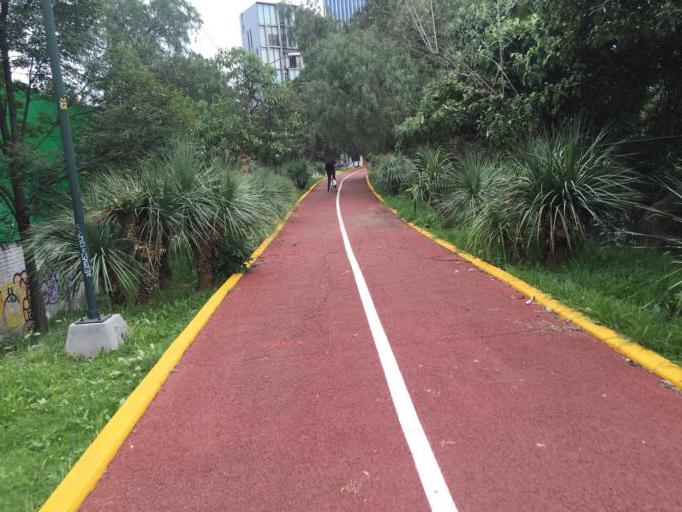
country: MX
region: Mexico City
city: Polanco
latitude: 19.4229
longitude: -99.2019
